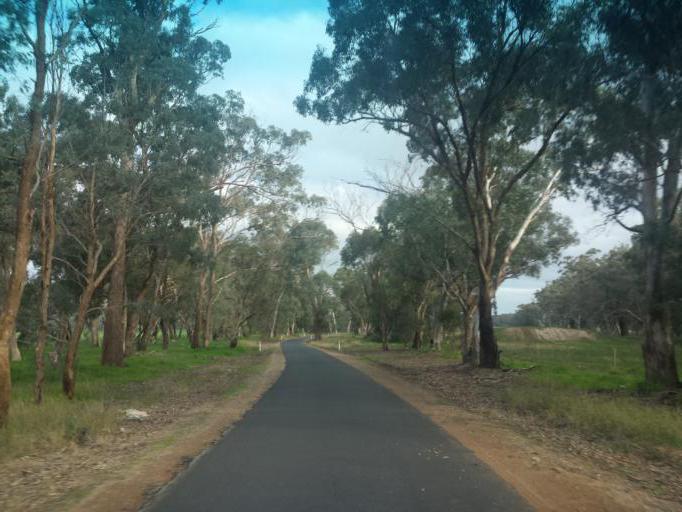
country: AU
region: Victoria
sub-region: Murrindindi
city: Kinglake West
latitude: -36.9186
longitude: 145.2257
